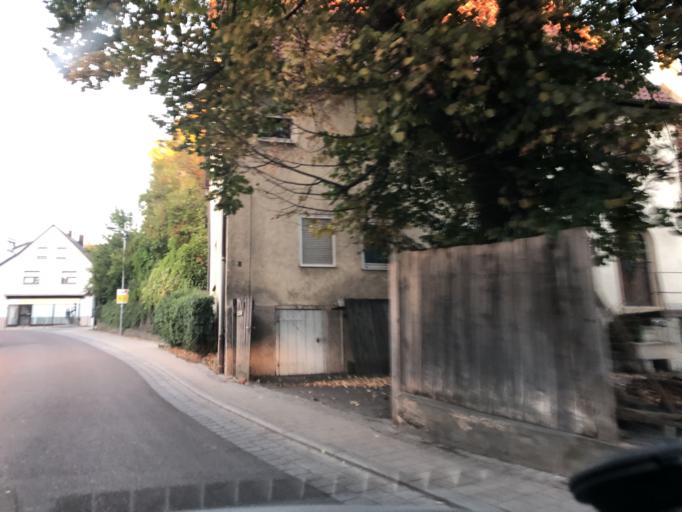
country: DE
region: Baden-Wuerttemberg
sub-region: Regierungsbezirk Stuttgart
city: Freiberg am Neckar
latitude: 48.9090
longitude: 9.2225
